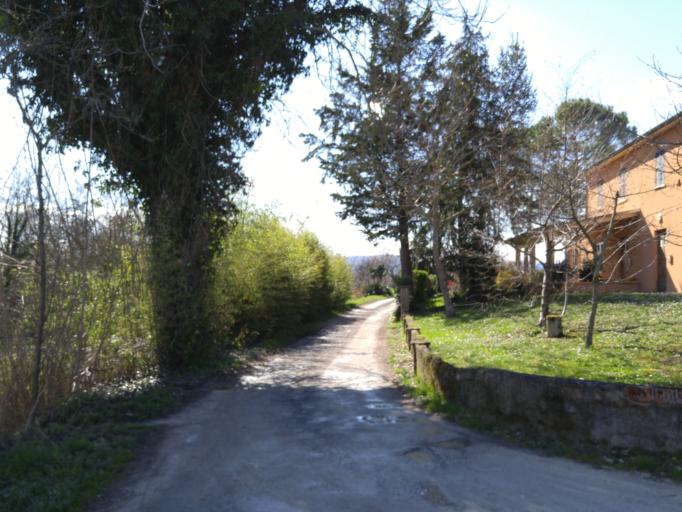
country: IT
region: The Marches
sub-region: Provincia di Pesaro e Urbino
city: Calcinelli
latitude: 43.7397
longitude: 12.9139
